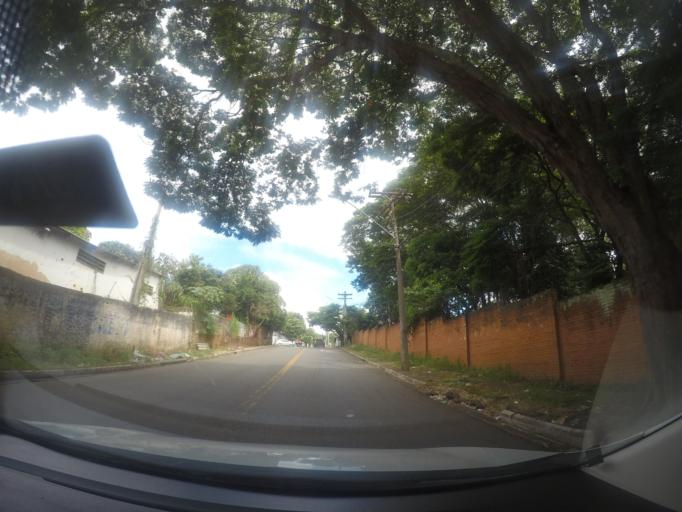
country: BR
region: Goias
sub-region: Goiania
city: Goiania
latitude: -16.6619
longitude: -49.2976
